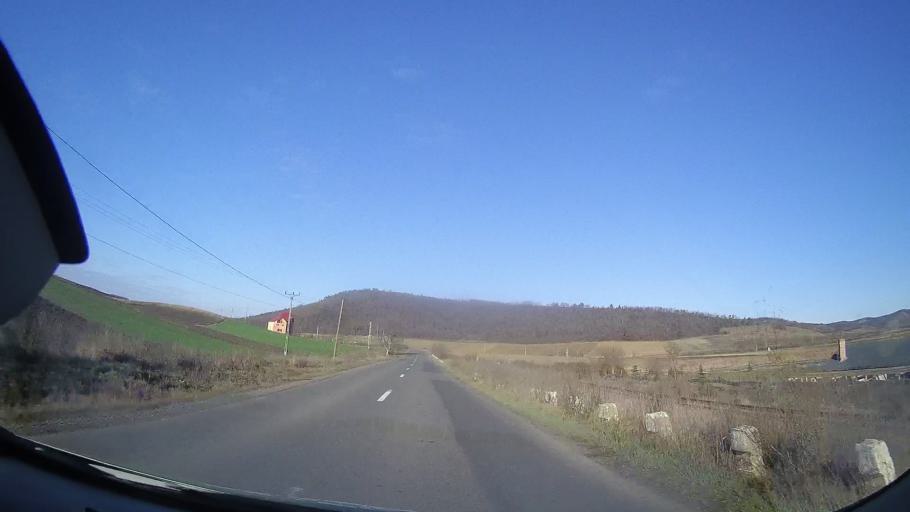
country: RO
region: Mures
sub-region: Comuna Mihesu de Campie
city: Mihesu de Campie
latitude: 46.6672
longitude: 24.1734
